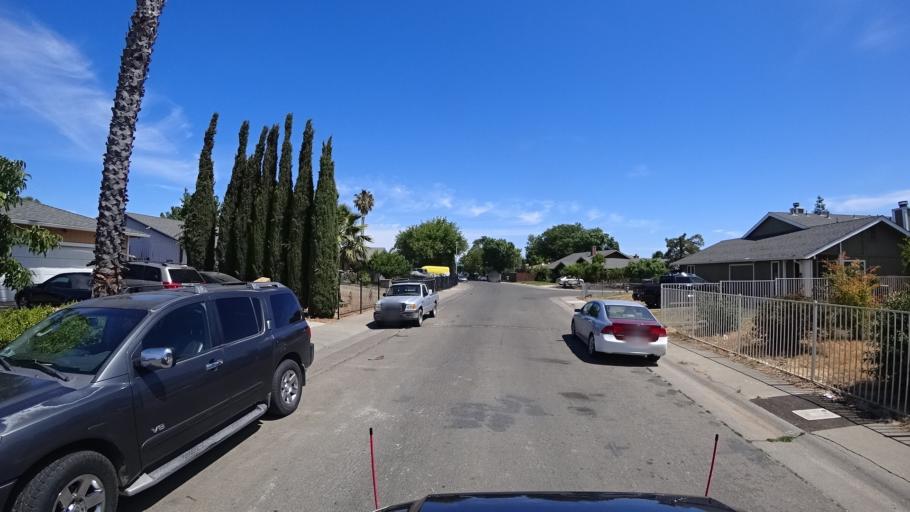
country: US
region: California
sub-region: Sacramento County
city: Florin
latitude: 38.5172
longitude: -121.4236
